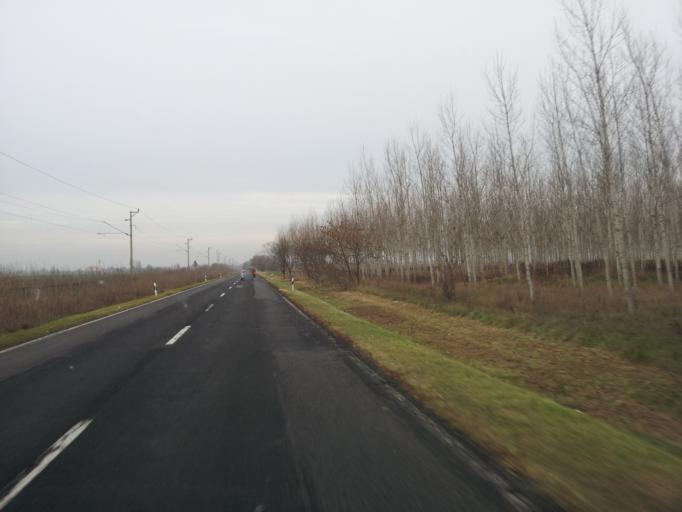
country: HU
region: Veszprem
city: Devecser
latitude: 47.1209
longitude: 17.4016
